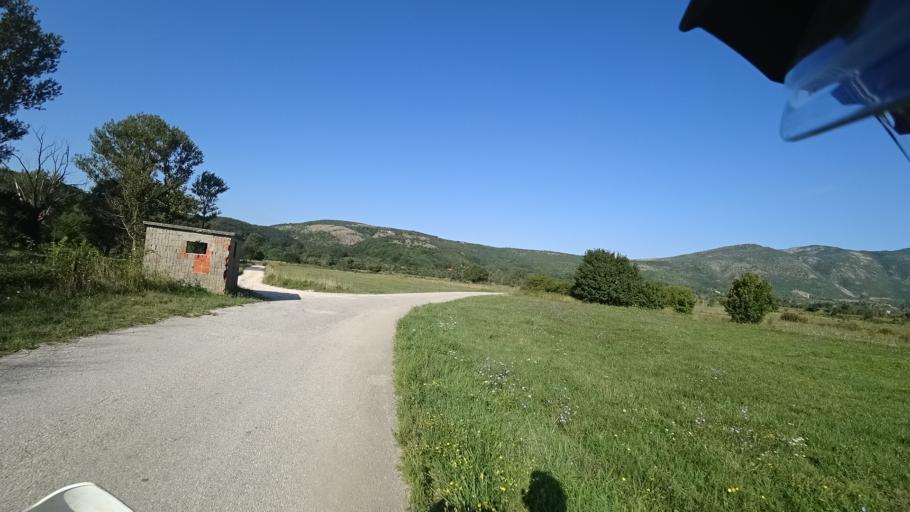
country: HR
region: Sibensko-Kniniska
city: Knin
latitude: 44.1479
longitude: 16.1658
